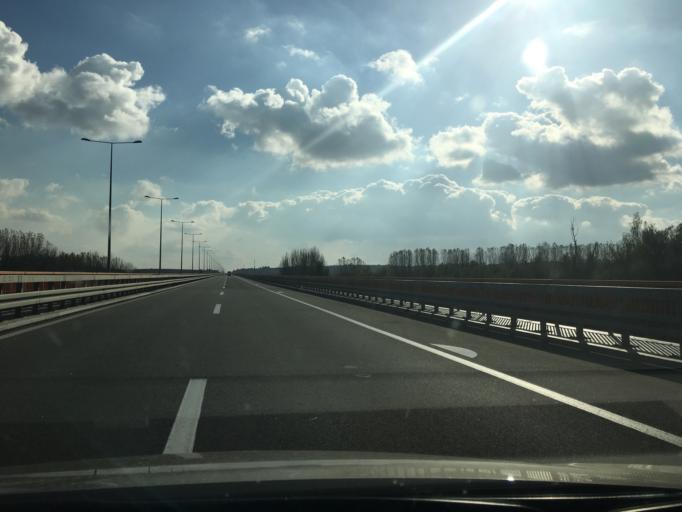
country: RS
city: Beska
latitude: 45.1839
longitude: 20.0773
